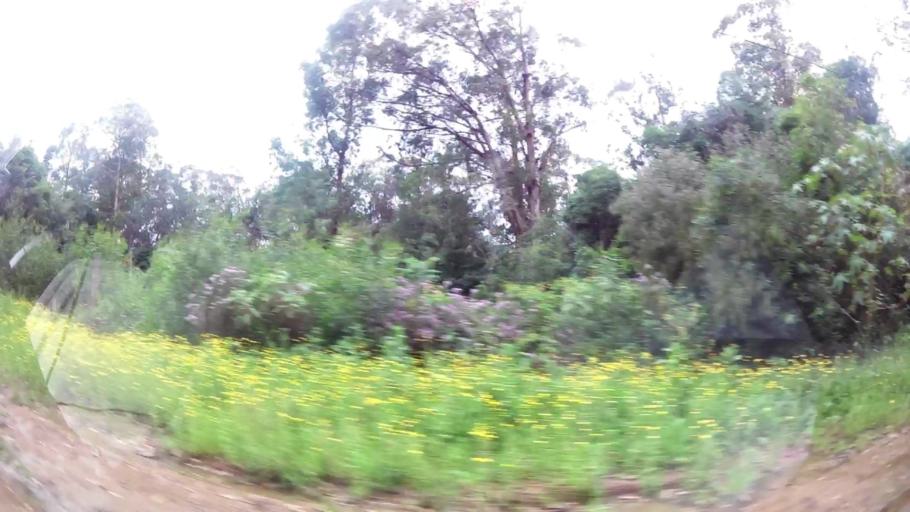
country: UY
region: Maldonado
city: Maldonado
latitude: -34.9036
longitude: -55.0387
